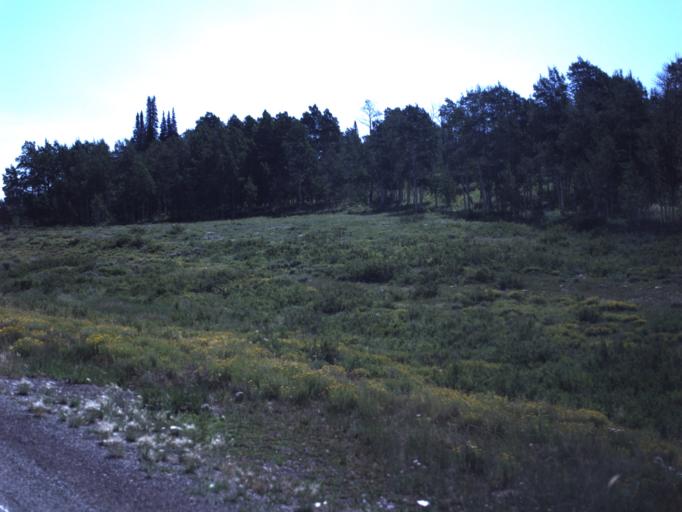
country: US
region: Utah
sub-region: Sanpete County
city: Fairview
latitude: 39.6782
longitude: -111.3184
